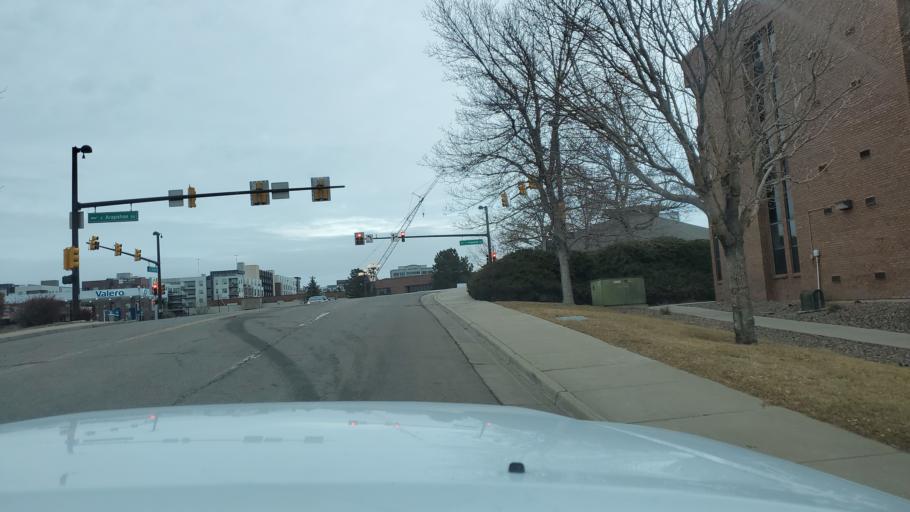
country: US
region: Colorado
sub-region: Arapahoe County
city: Castlewood
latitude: 39.5945
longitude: -104.8979
